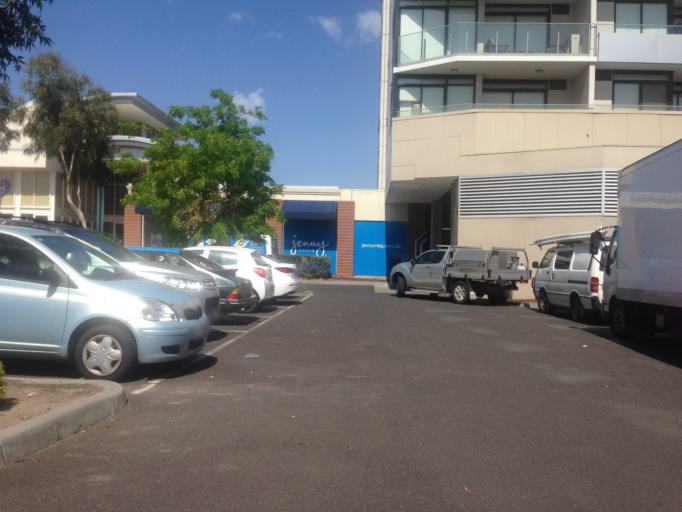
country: AU
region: Victoria
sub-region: Darebin
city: Northcote
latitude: -37.7682
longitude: 145.0027
